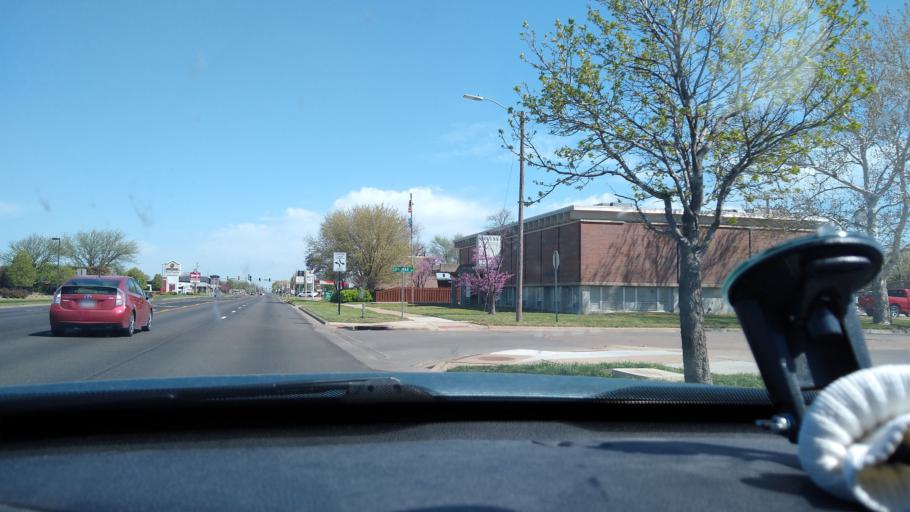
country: US
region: Kansas
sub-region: Saline County
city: Salina
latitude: 38.8064
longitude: -97.5942
